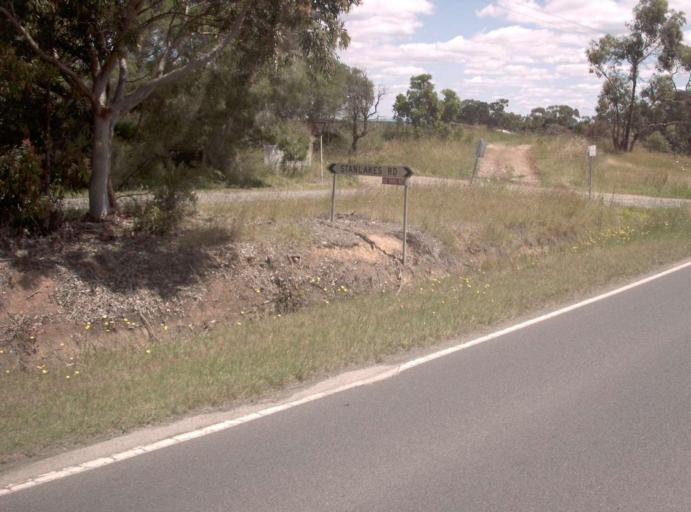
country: AU
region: Victoria
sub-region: Cardinia
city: Koo-Wee-Rup
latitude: -38.2851
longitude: 145.5467
